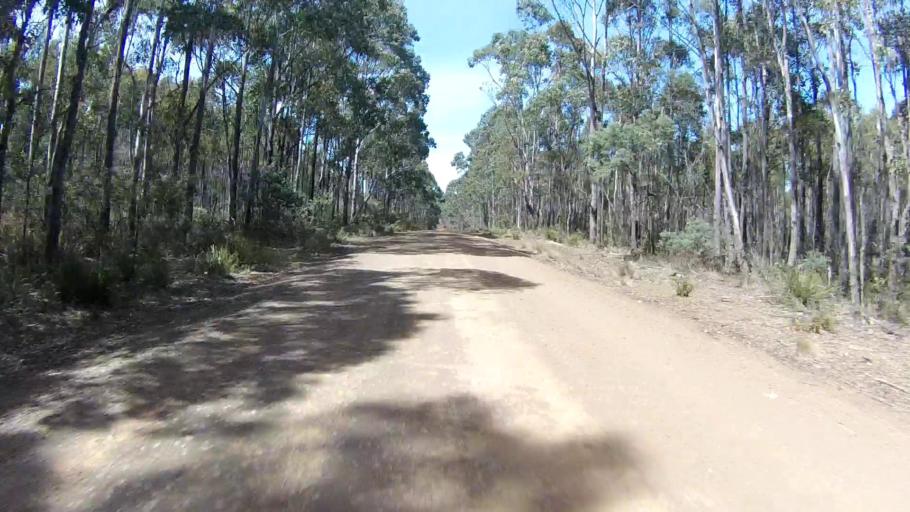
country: AU
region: Tasmania
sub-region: Sorell
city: Sorell
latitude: -42.6795
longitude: 147.7311
